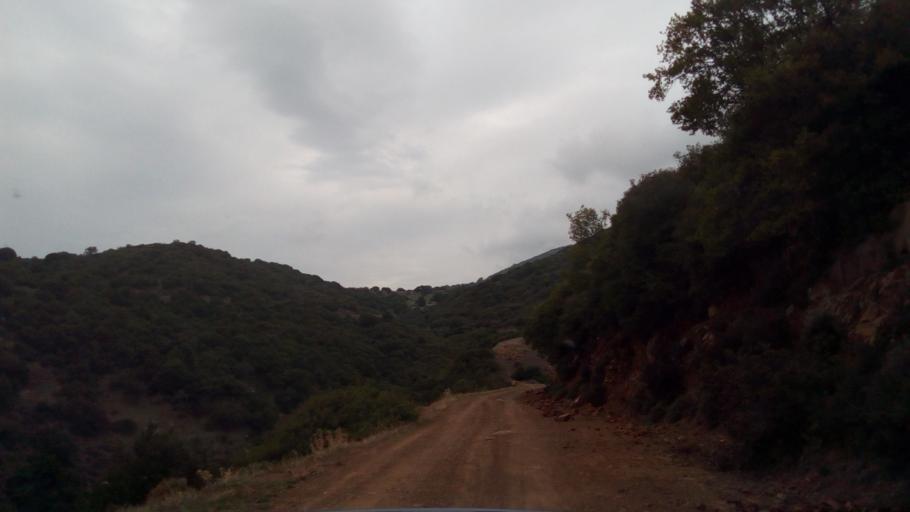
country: GR
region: West Greece
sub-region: Nomos Achaias
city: Aigio
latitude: 38.3746
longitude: 22.1561
